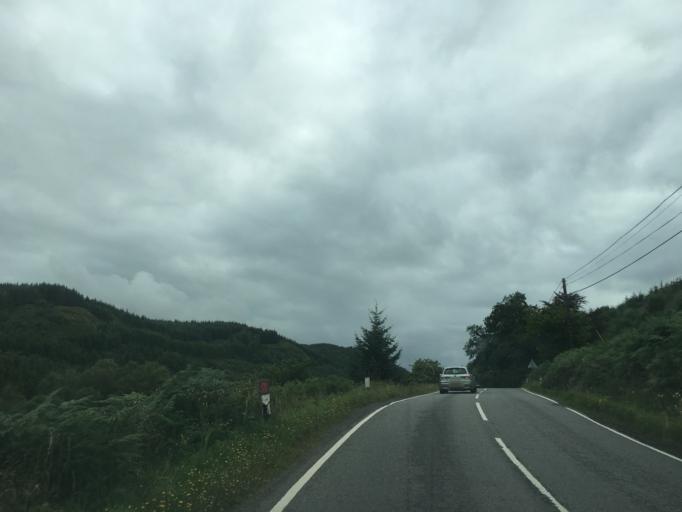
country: GB
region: Scotland
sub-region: Argyll and Bute
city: Oban
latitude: 56.2987
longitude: -5.4633
